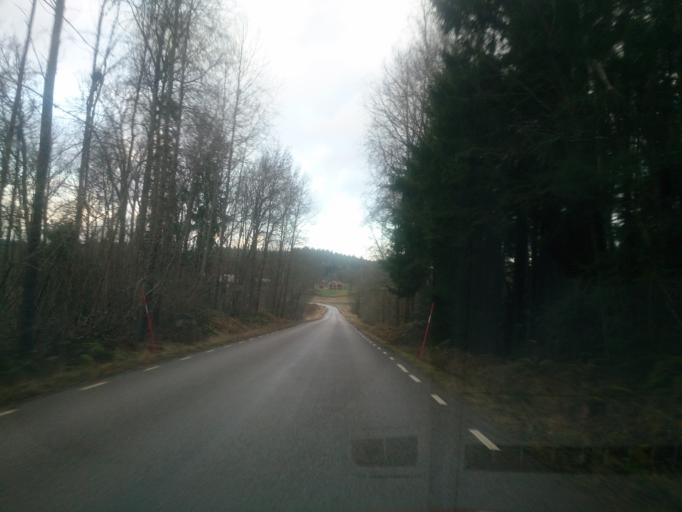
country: SE
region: OEstergoetland
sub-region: Atvidabergs Kommun
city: Atvidaberg
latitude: 58.2822
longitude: 16.0361
